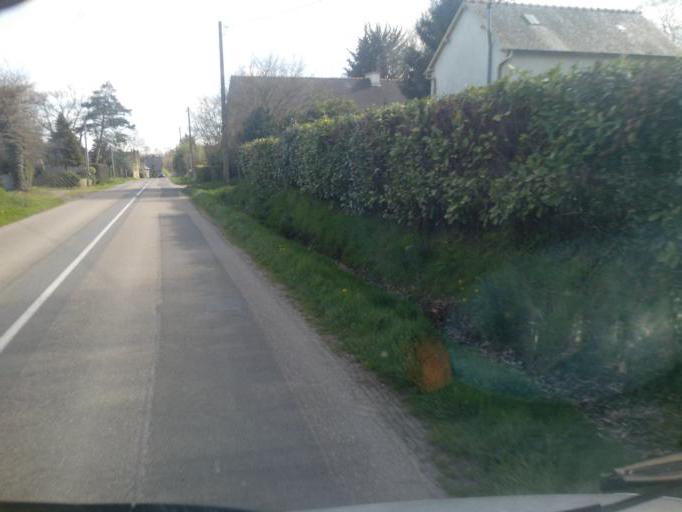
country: FR
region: Brittany
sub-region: Departement d'Ille-et-Vilaine
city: Maxent
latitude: 47.9658
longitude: -2.0163
